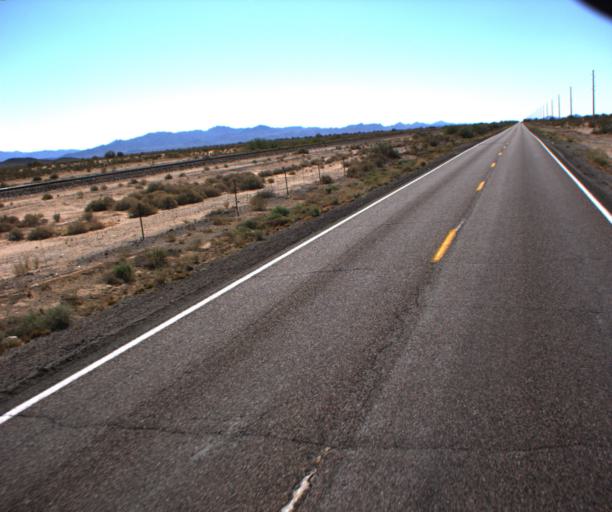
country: US
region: Arizona
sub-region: La Paz County
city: Quartzsite
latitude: 33.8888
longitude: -113.9568
